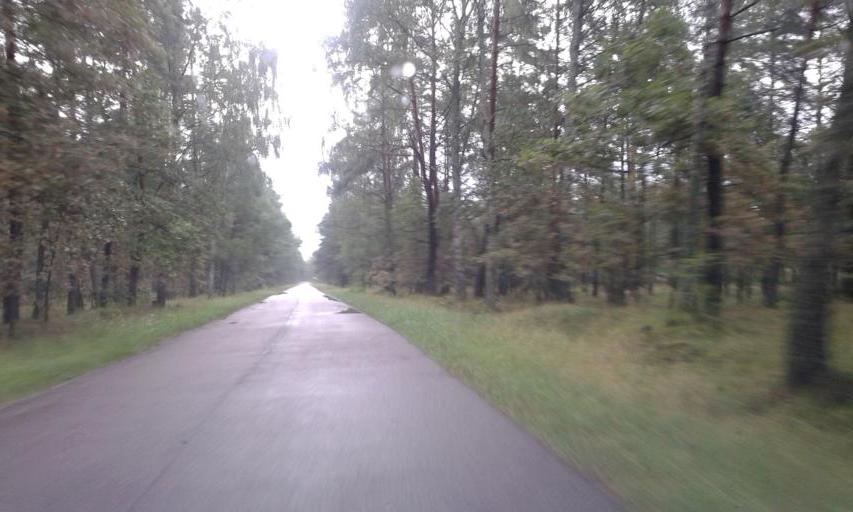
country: PL
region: West Pomeranian Voivodeship
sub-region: Powiat szczecinecki
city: Borne Sulinowo
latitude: 53.5373
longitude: 16.5023
